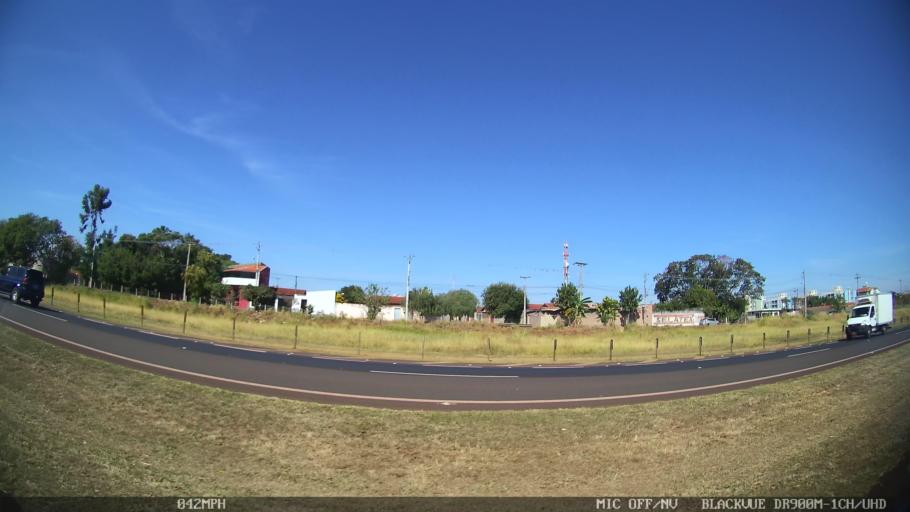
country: BR
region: Sao Paulo
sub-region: Ribeirao Preto
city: Ribeirao Preto
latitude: -21.1313
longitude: -47.8524
